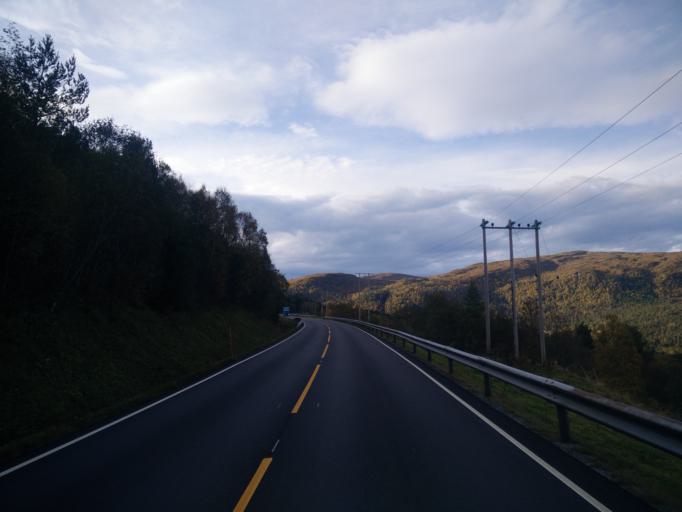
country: NO
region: More og Romsdal
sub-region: Gjemnes
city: Batnfjordsora
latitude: 62.8574
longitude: 7.6054
